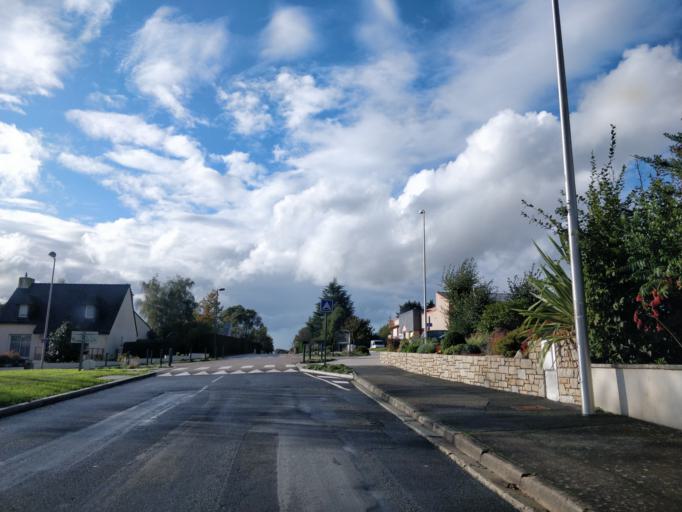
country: FR
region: Brittany
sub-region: Departement d'Ille-et-Vilaine
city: Servon-sur-Vilaine
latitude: 48.1240
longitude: -1.4652
